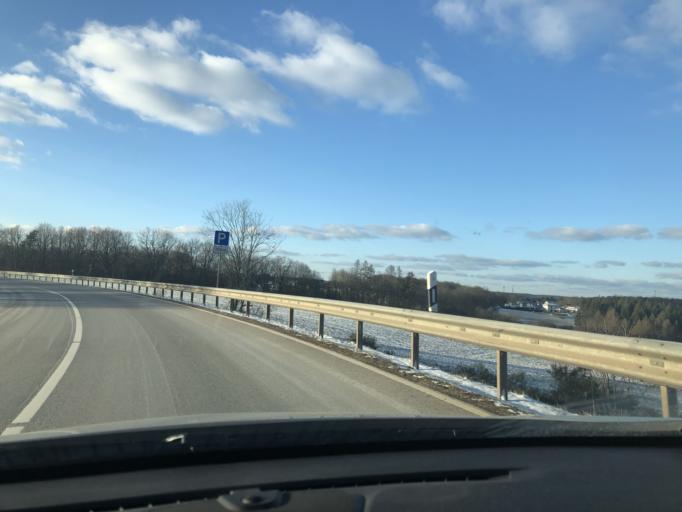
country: DE
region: Rheinland-Pfalz
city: Hasborn
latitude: 50.0464
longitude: 6.9173
